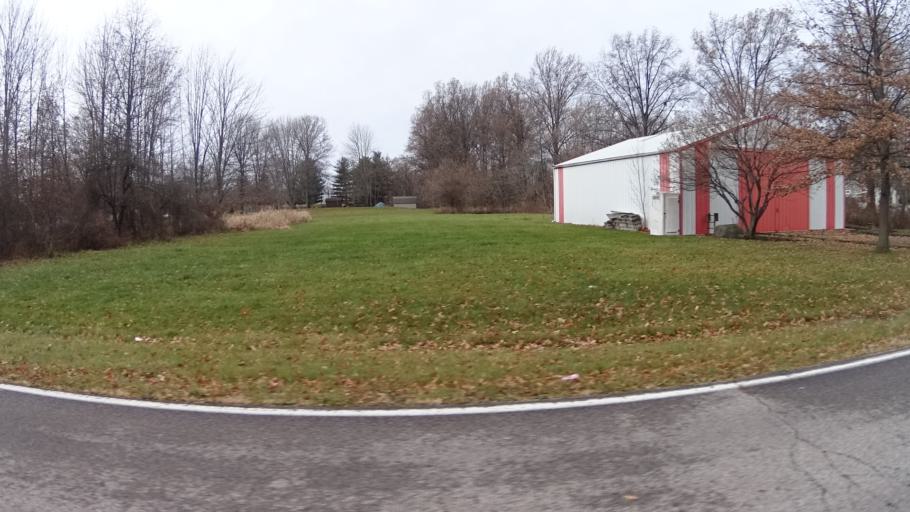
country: US
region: Ohio
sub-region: Lorain County
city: North Ridgeville
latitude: 41.3726
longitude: -82.0343
